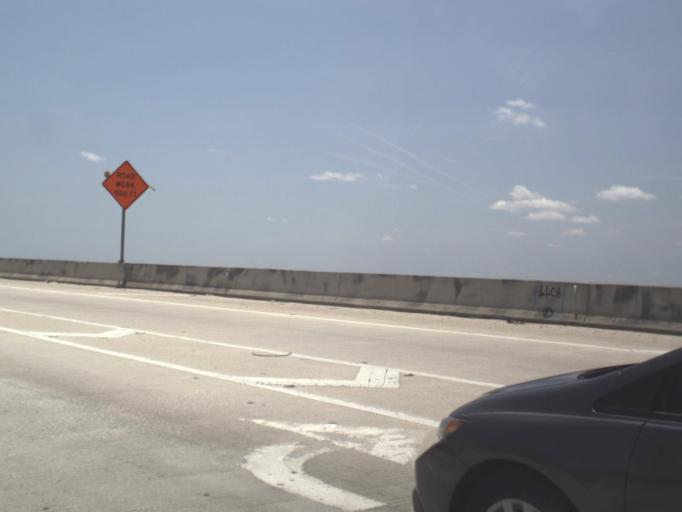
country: US
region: Florida
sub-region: Duval County
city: Jacksonville
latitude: 30.3158
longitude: -81.6740
